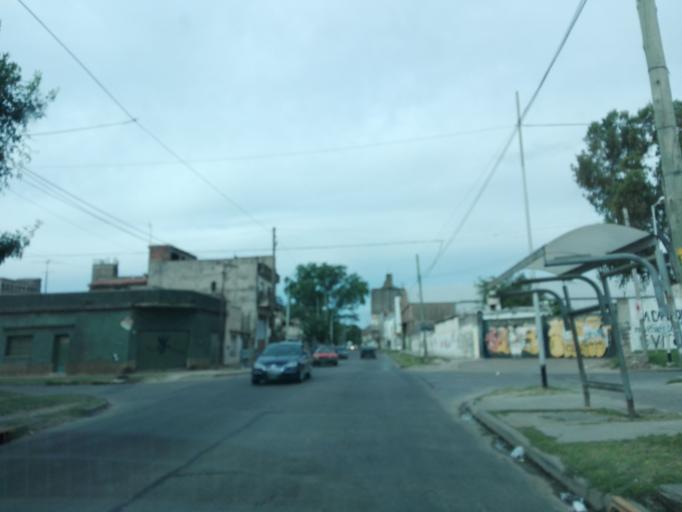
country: AR
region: Buenos Aires
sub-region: Partido de Lanus
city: Lanus
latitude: -34.6995
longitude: -58.3627
